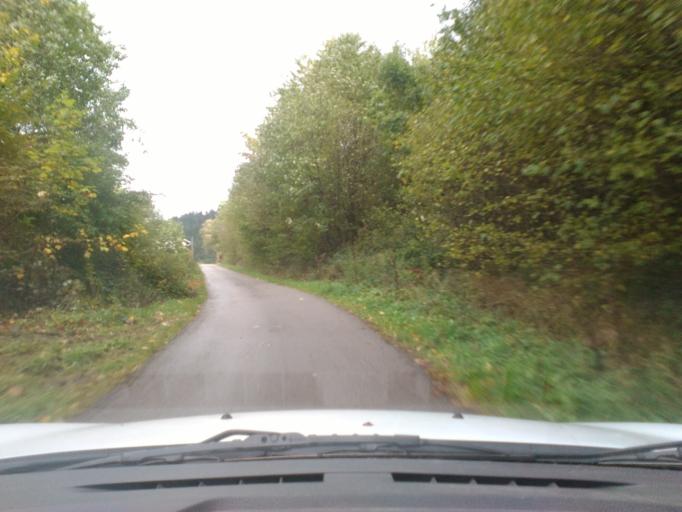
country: FR
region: Lorraine
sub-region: Departement des Vosges
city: Saint-Die-des-Vosges
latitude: 48.3120
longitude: 6.9794
